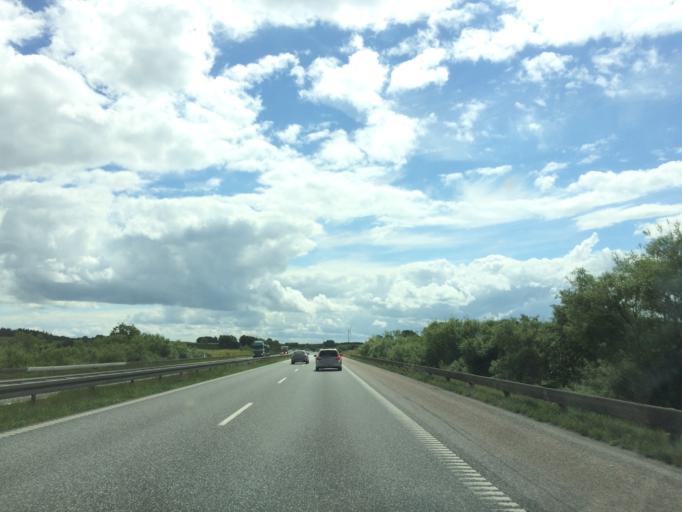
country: DK
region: North Denmark
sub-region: Mariagerfjord Kommune
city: Hobro
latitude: 56.6995
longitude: 9.7291
